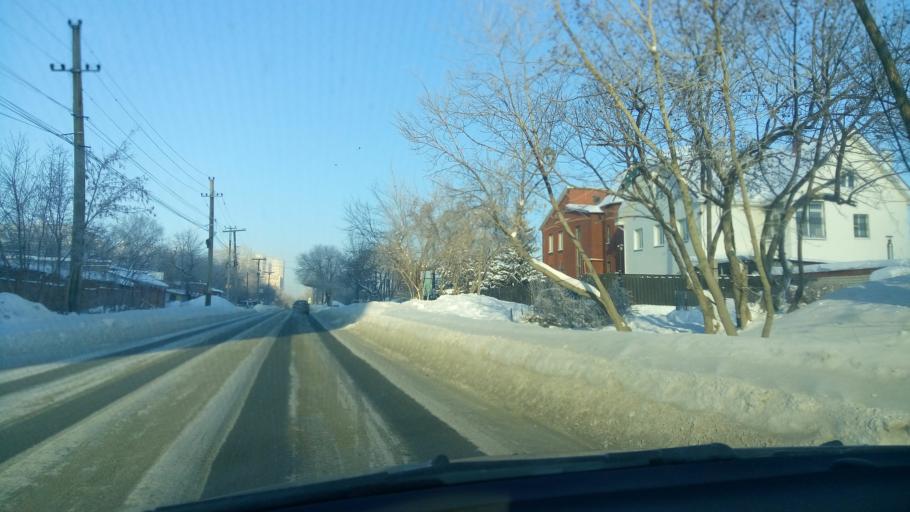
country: RU
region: Chelyabinsk
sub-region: Gorod Chelyabinsk
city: Chelyabinsk
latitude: 55.1280
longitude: 61.3807
